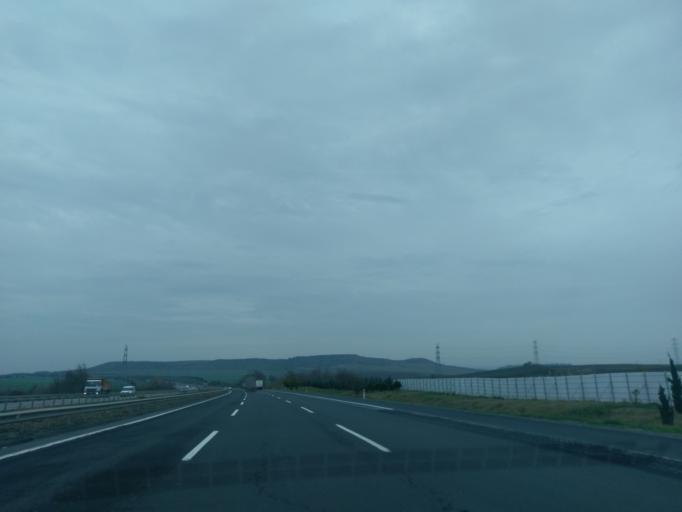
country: TR
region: Istanbul
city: Canta
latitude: 41.1488
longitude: 28.1461
